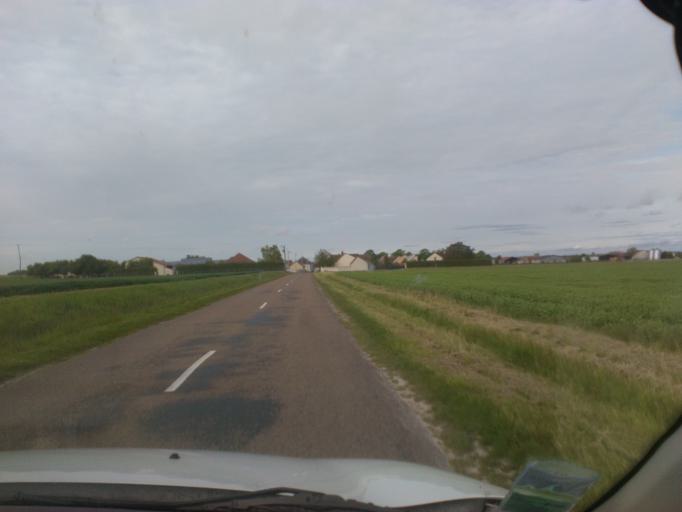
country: FR
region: Champagne-Ardenne
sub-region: Departement de l'Aube
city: Marigny-le-Chatel
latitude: 48.3796
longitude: 3.7851
